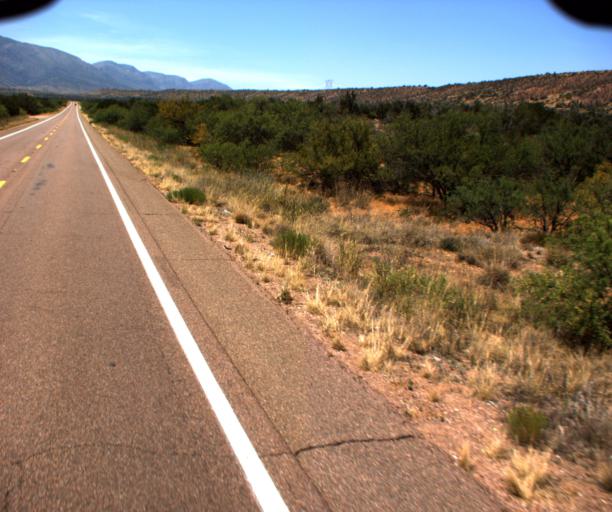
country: US
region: Arizona
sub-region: Gila County
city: Tonto Basin
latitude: 34.0200
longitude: -111.3350
